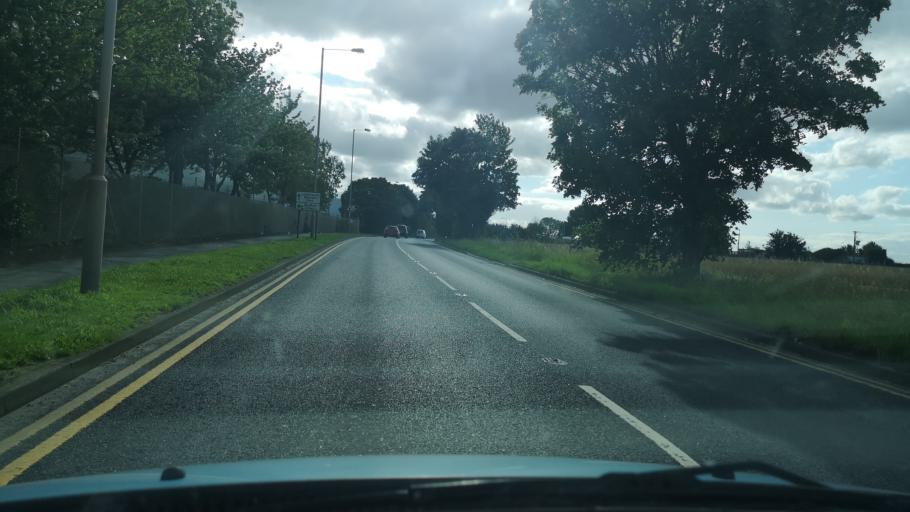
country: GB
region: England
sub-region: City and Borough of Wakefield
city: North Elmsall
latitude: 53.6051
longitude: -1.2805
